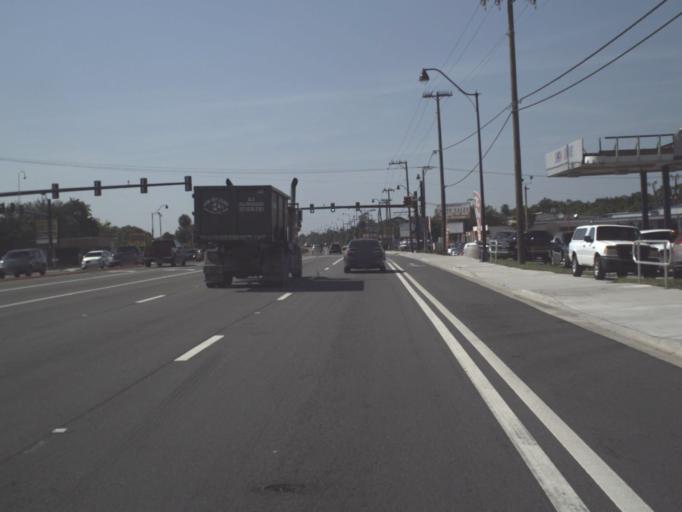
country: US
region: Florida
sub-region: Brevard County
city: Cocoa
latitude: 28.3773
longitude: -80.7381
